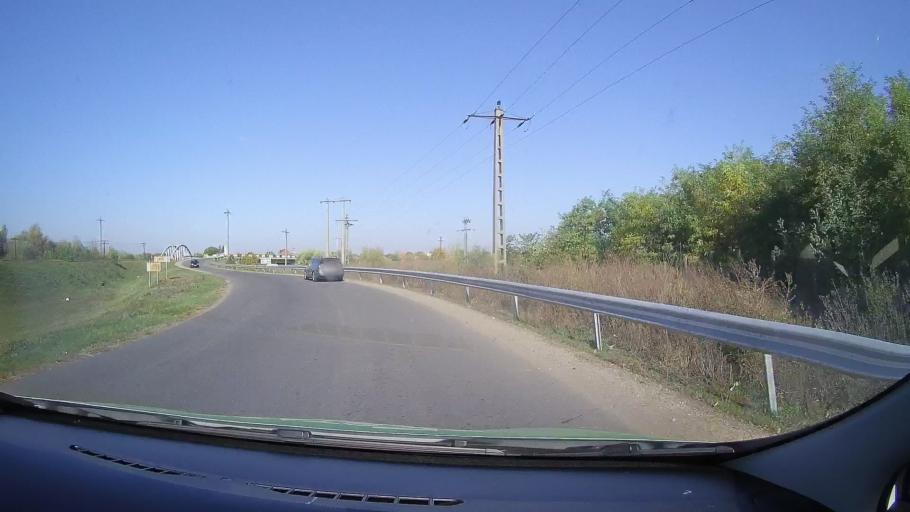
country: RO
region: Satu Mare
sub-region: Comuna Berveni
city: Lucaceni
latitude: 47.7471
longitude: 22.4742
